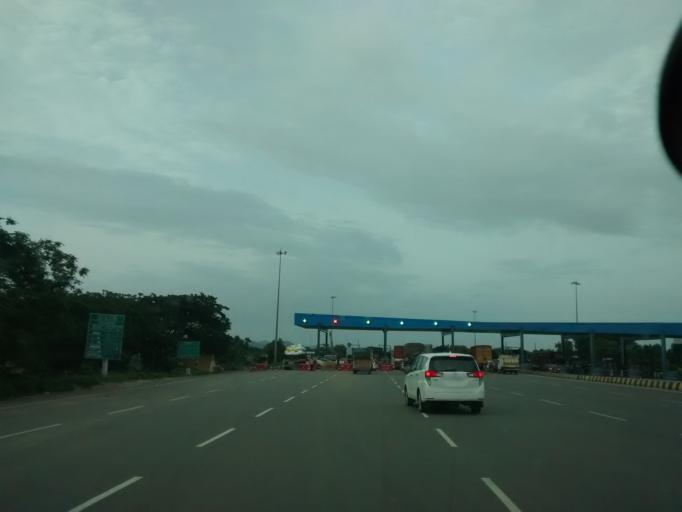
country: IN
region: Telangana
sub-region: Mahbubnagar
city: Gopalur
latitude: 16.5349
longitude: 77.9440
